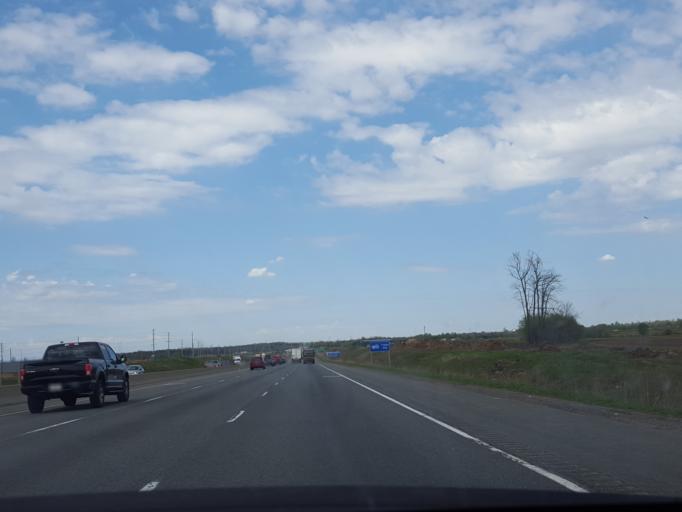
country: CA
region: Ontario
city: Oshawa
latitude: 43.8823
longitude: -78.7370
